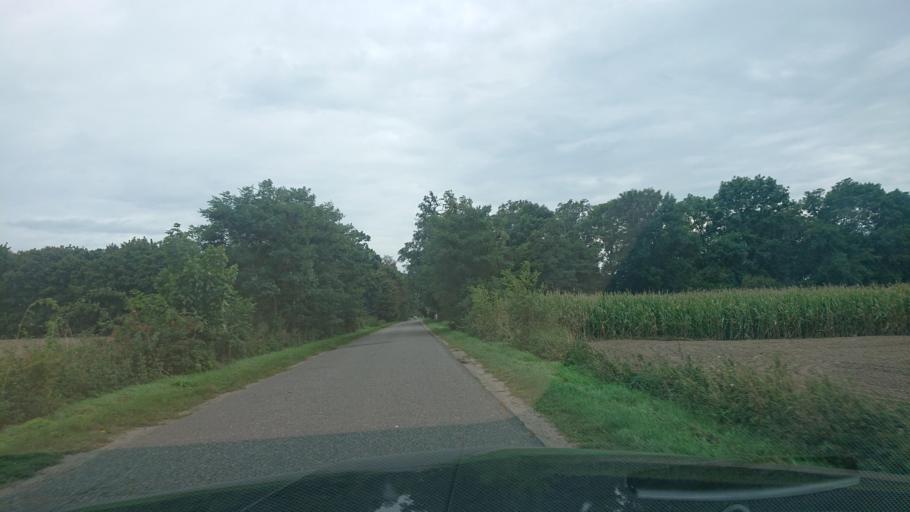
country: PL
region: Greater Poland Voivodeship
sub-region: Powiat gnieznienski
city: Niechanowo
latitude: 52.4586
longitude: 17.6197
